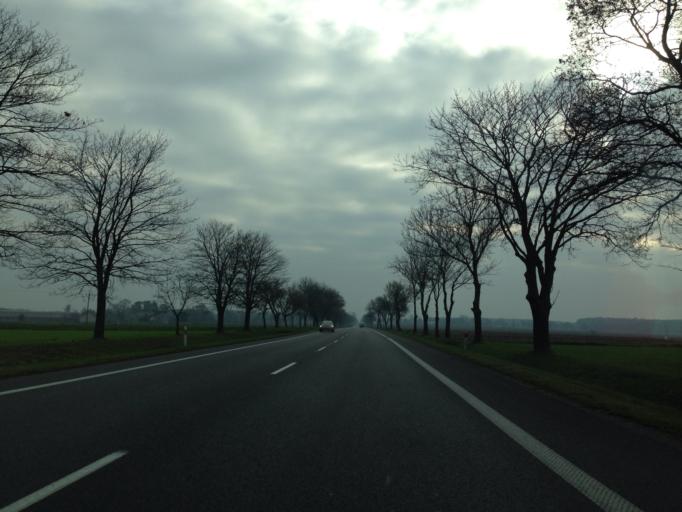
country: PL
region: Masovian Voivodeship
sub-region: Powiat sierpecki
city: Zawidz
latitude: 52.7945
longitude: 19.8699
